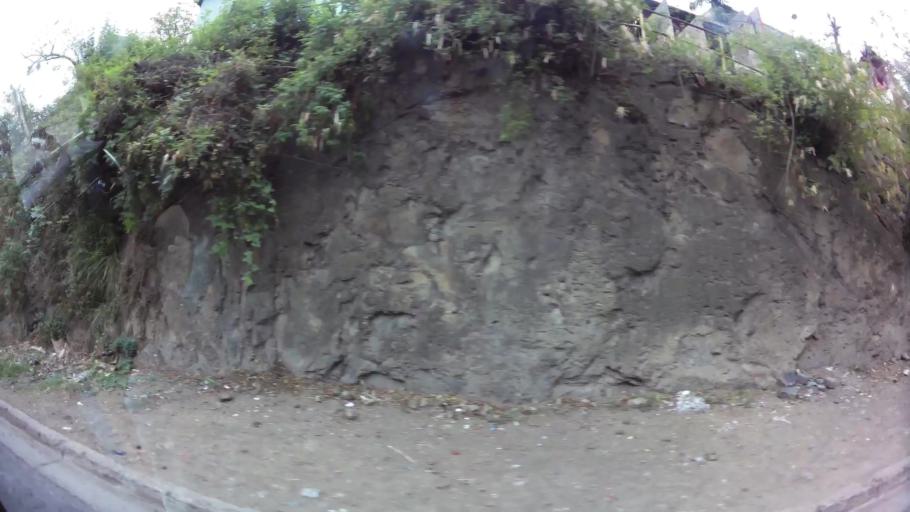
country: NI
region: Matagalpa
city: Matagalpa
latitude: 12.9312
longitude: -85.9183
